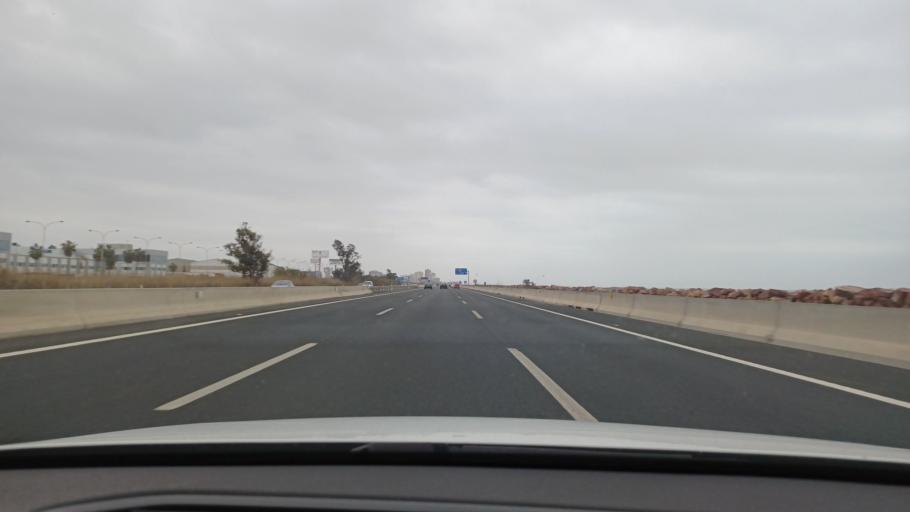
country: ES
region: Valencia
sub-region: Provincia de Valencia
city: Albuixech
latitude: 39.5416
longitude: -0.3030
